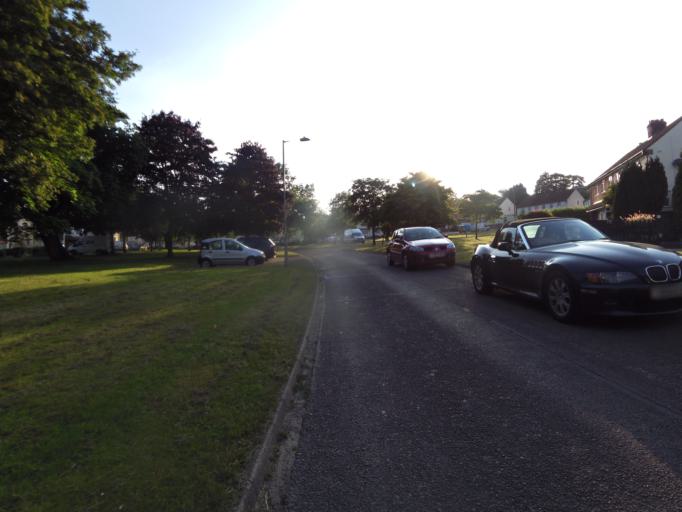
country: GB
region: England
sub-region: Suffolk
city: Ipswich
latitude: 52.0440
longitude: 1.1464
